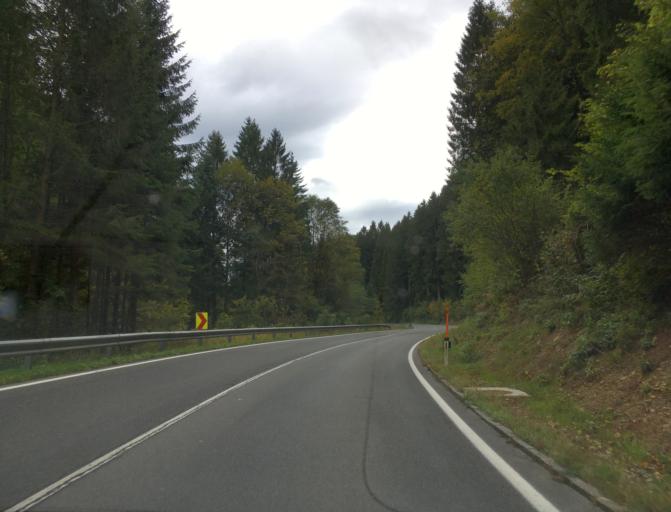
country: AT
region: Lower Austria
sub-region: Politischer Bezirk Neunkirchen
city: Thomasberg
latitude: 47.5579
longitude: 16.1431
